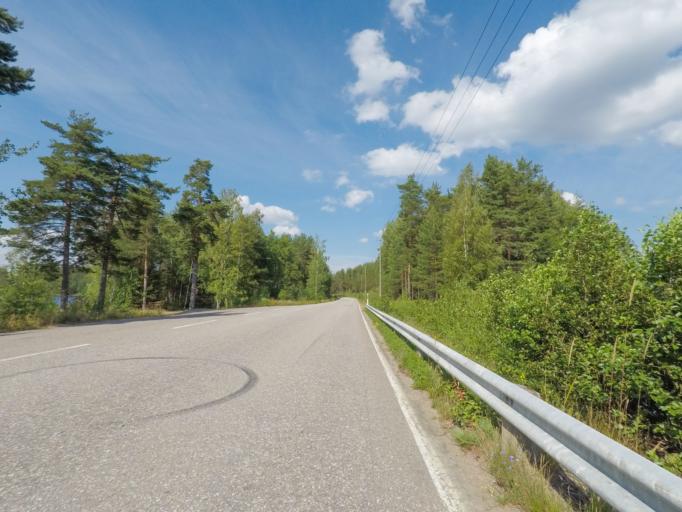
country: FI
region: Southern Savonia
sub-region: Mikkeli
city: Puumala
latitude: 61.4916
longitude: 28.1672
